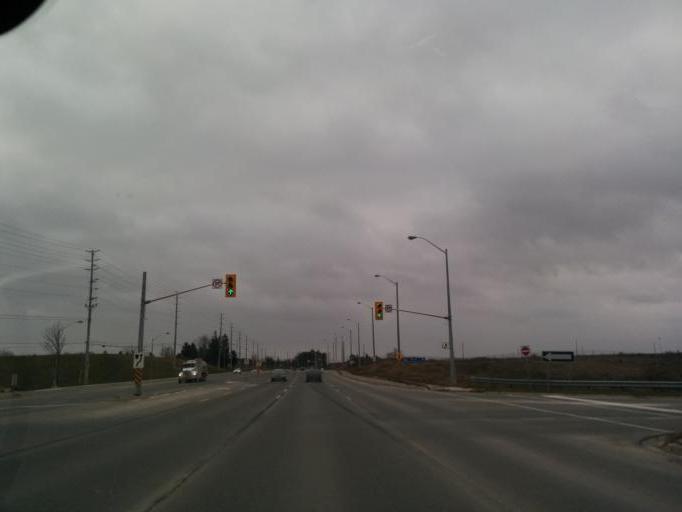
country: CA
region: Ontario
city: Brampton
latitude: 43.7554
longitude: -79.8004
